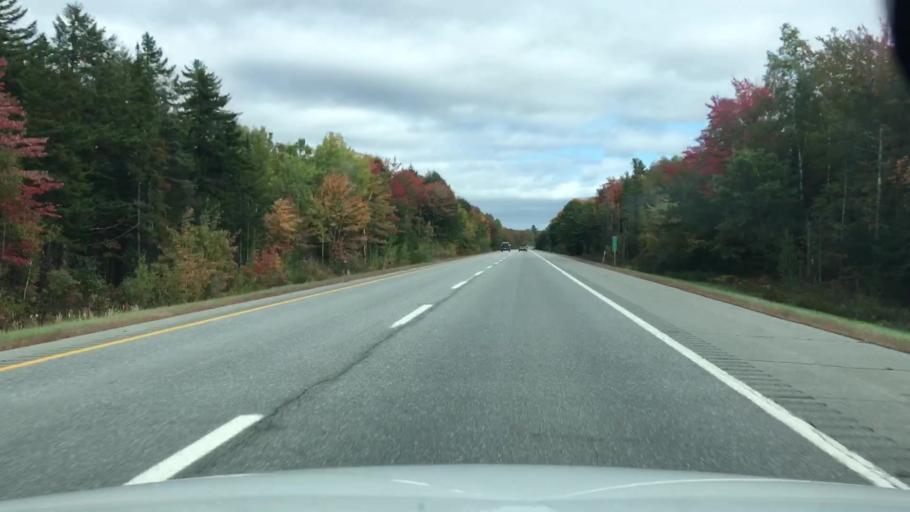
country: US
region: Maine
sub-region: Penobscot County
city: Carmel
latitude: 44.7736
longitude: -69.0258
